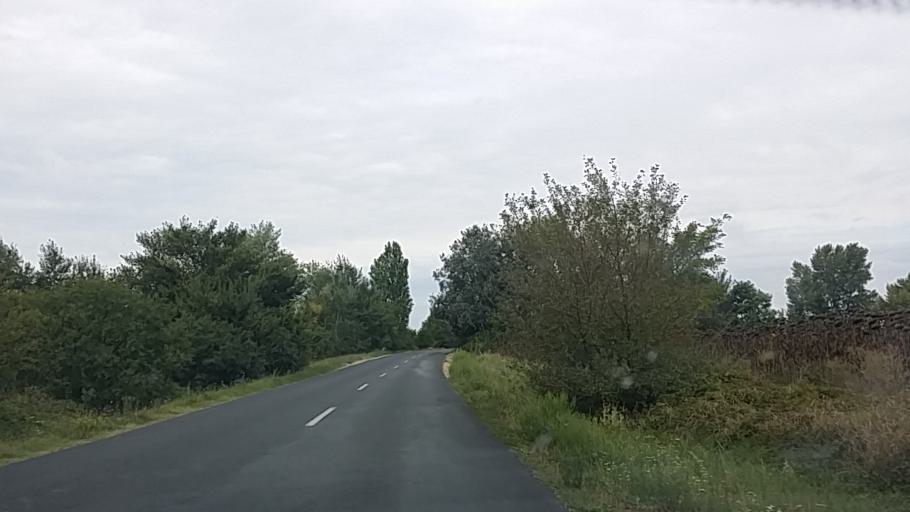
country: HU
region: Komarom-Esztergom
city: Mocsa
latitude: 47.7134
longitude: 18.1904
